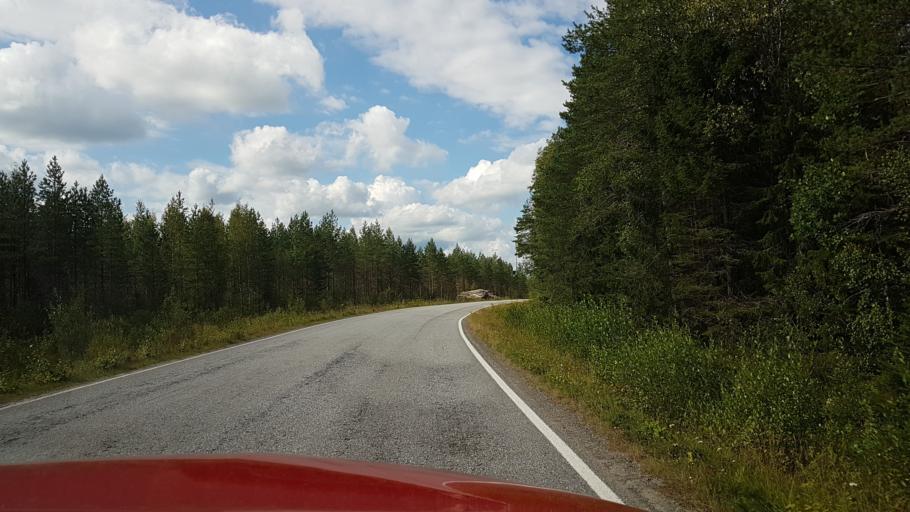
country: FI
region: Northern Ostrobothnia
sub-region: Ylivieska
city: Himanka
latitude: 64.0712
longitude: 23.6953
